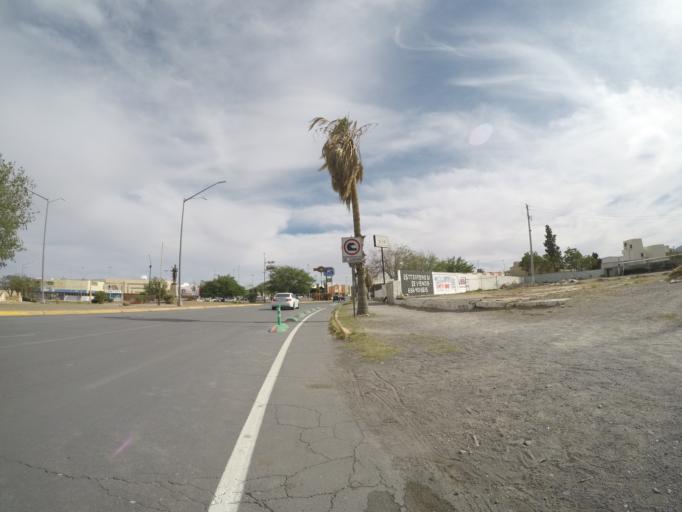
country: MX
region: Chihuahua
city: Ciudad Juarez
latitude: 31.7429
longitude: -106.4533
